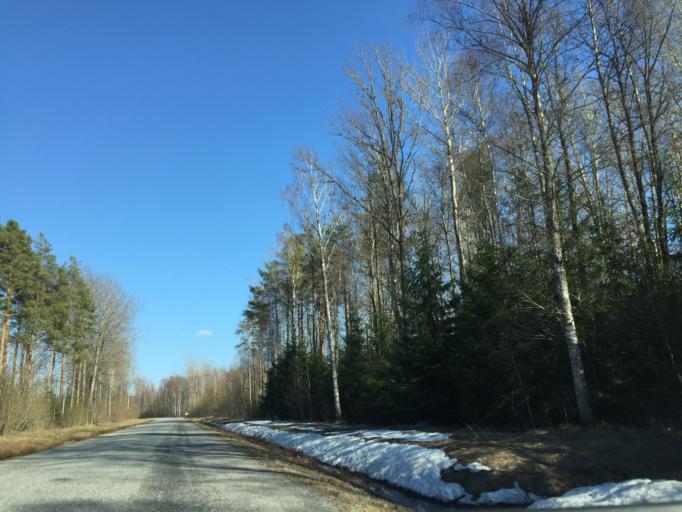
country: RU
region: Pskov
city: Gdov
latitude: 59.0111
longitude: 27.5908
